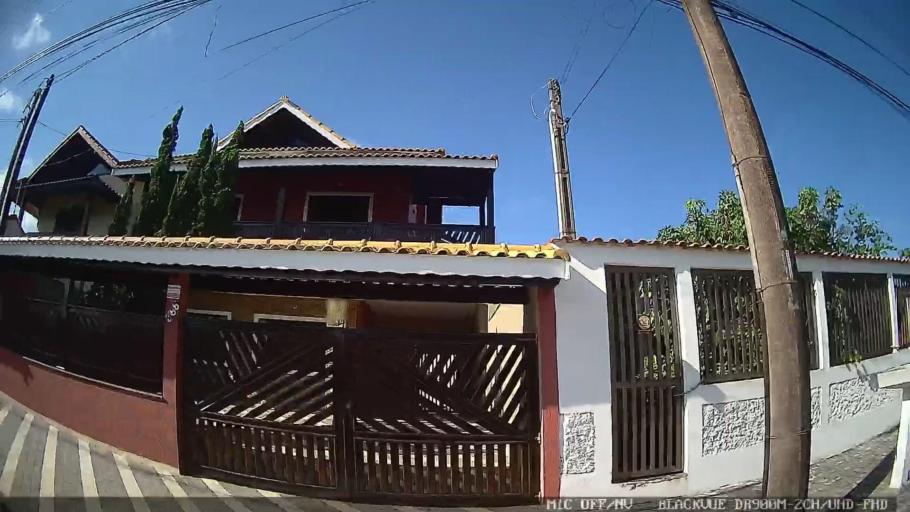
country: BR
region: Sao Paulo
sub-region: Peruibe
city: Peruibe
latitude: -24.2860
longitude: -46.9620
